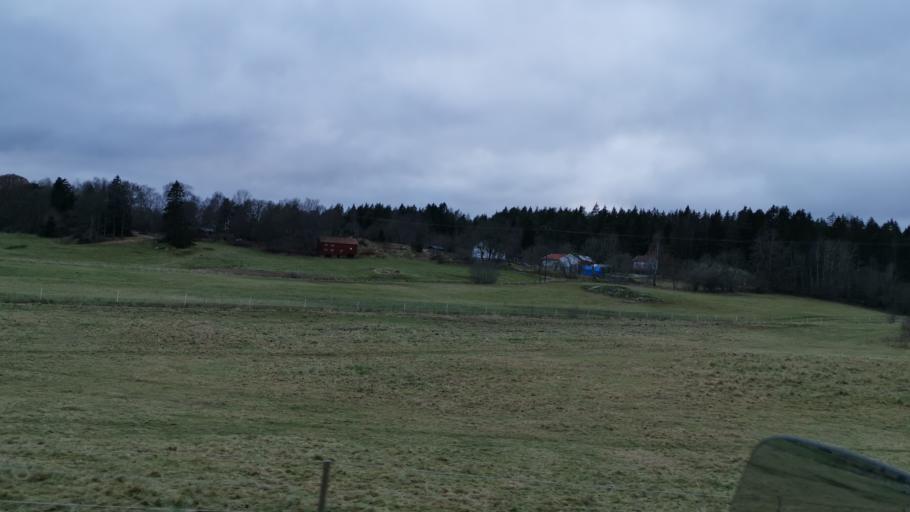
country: SE
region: Vaestra Goetaland
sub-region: Orust
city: Henan
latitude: 58.2274
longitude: 11.7005
